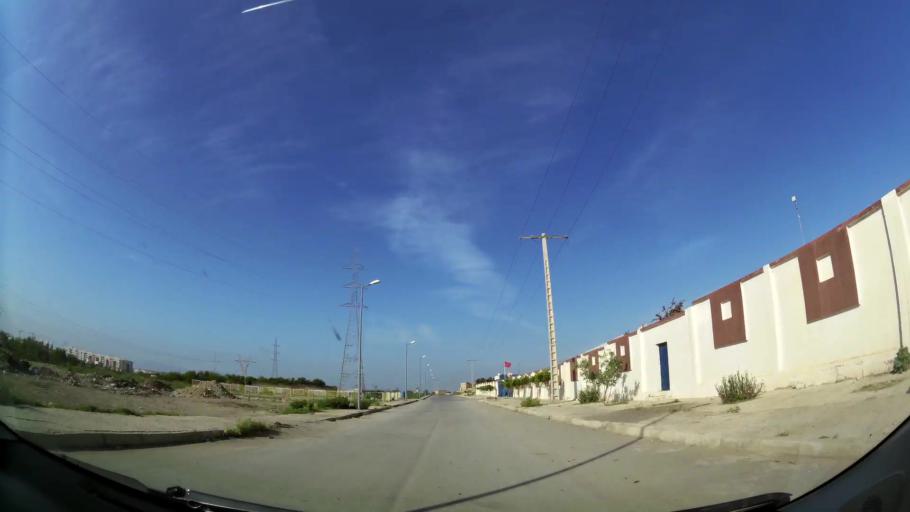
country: MA
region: Oriental
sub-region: Oujda-Angad
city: Oujda
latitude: 34.7149
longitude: -1.9102
